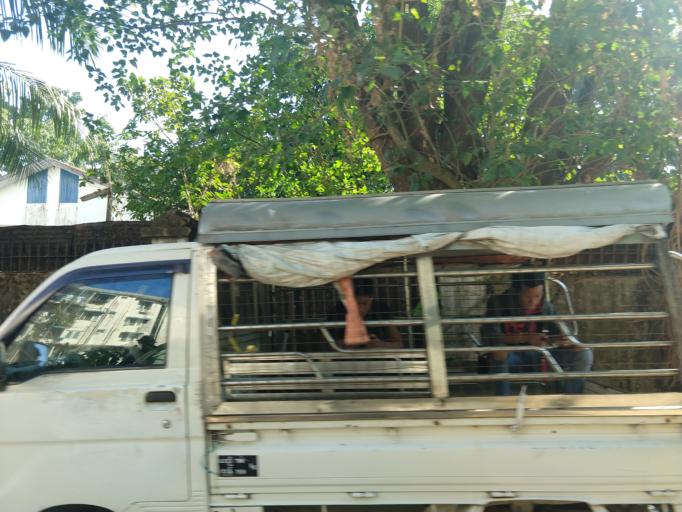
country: MM
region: Yangon
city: Yangon
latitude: 16.7923
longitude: 96.1766
